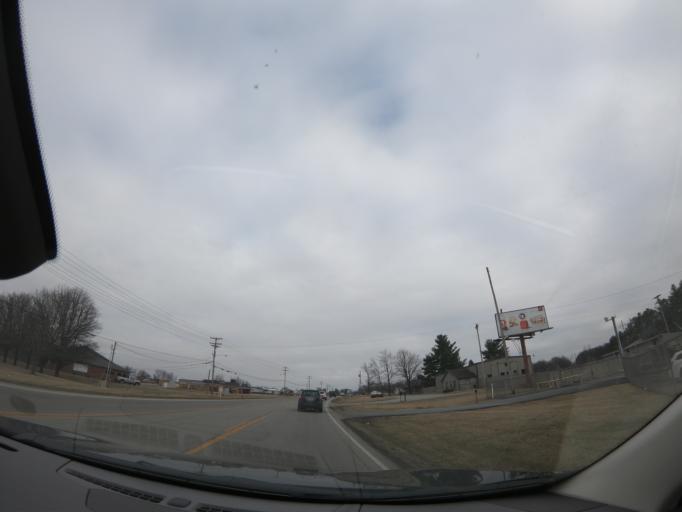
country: US
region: Kentucky
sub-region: Nelson County
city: Bardstown
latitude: 37.8245
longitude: -85.4410
